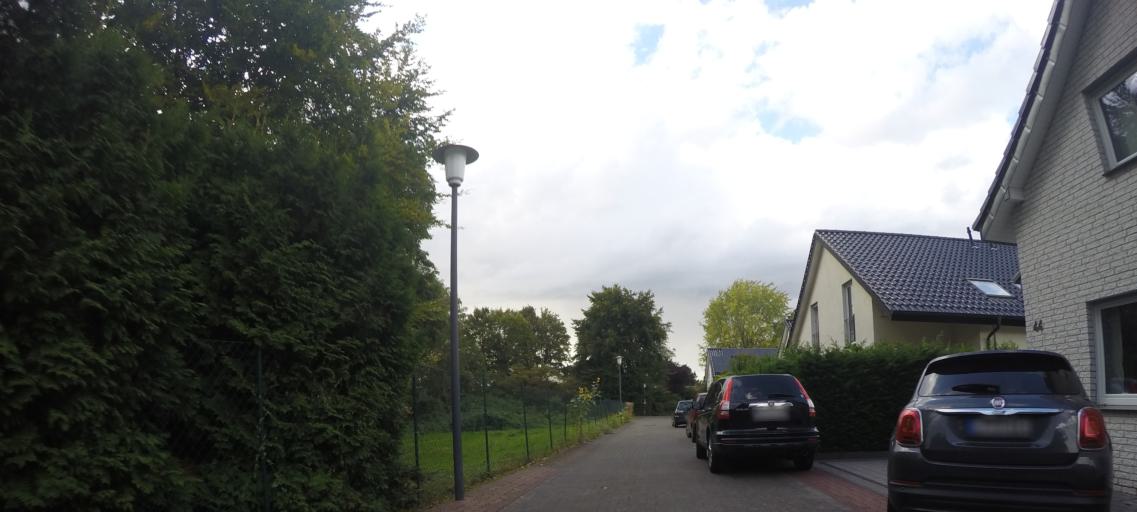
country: DE
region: North Rhine-Westphalia
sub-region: Regierungsbezirk Arnsberg
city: Lippstadt
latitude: 51.6833
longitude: 8.3562
